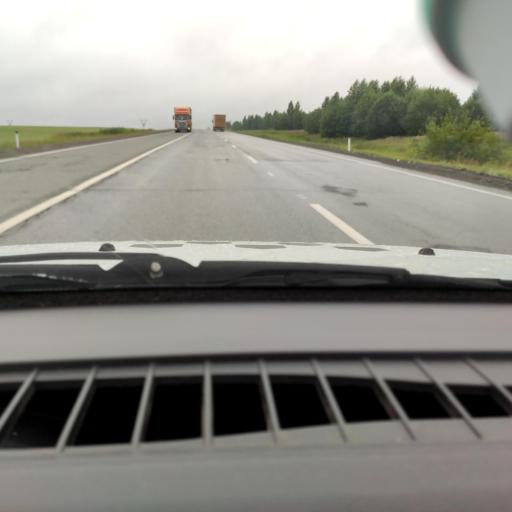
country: RU
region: Perm
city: Kungur
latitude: 57.3489
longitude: 56.9379
